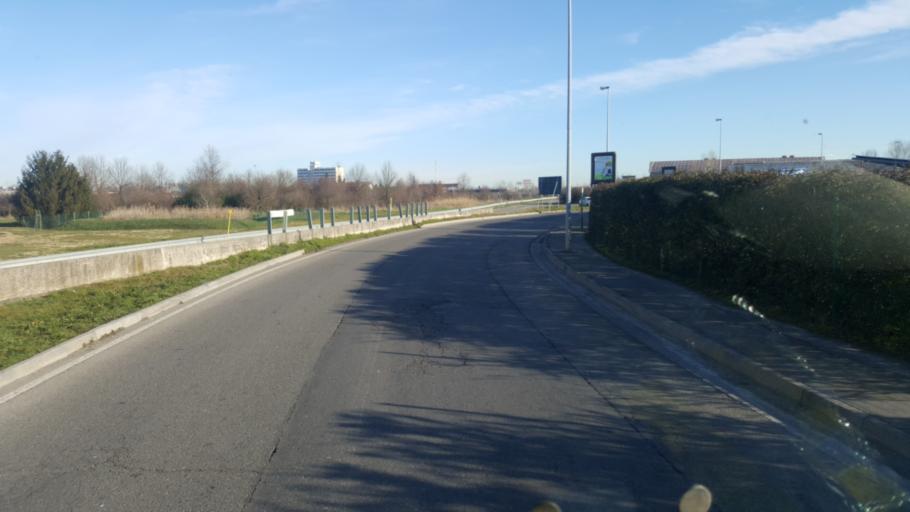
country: IT
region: Emilia-Romagna
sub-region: Provincia di Modena
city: Campogalliano
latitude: 44.6562
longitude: 10.8568
